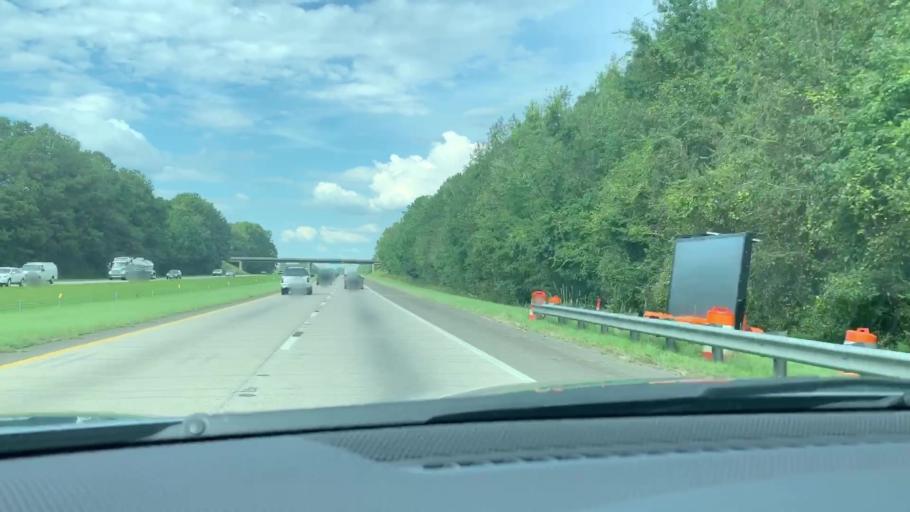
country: US
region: South Carolina
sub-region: Hampton County
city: Yemassee
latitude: 32.6758
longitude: -80.8825
